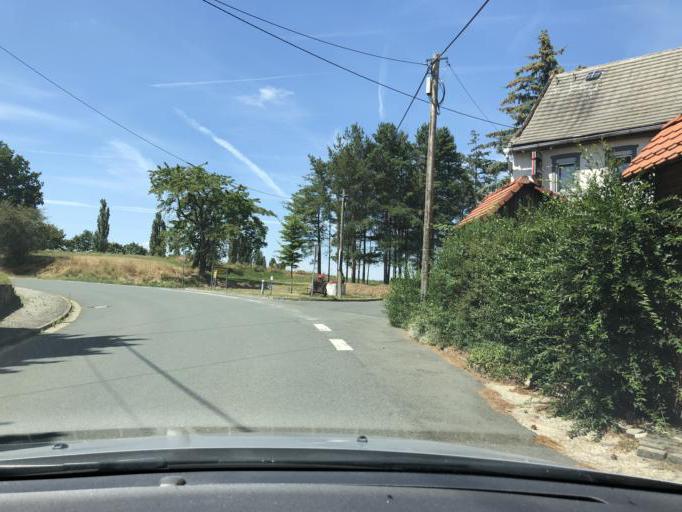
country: DE
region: Thuringia
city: Schkolen
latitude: 51.0651
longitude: 11.8384
